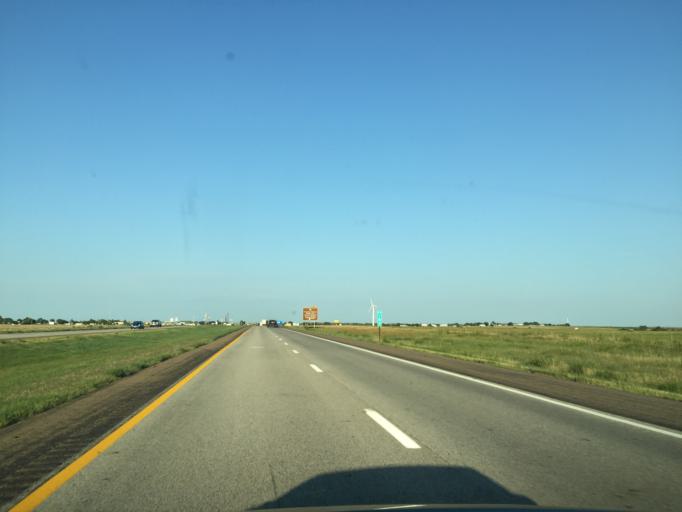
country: US
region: Kansas
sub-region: Russell County
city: Russell
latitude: 38.8640
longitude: -98.8729
